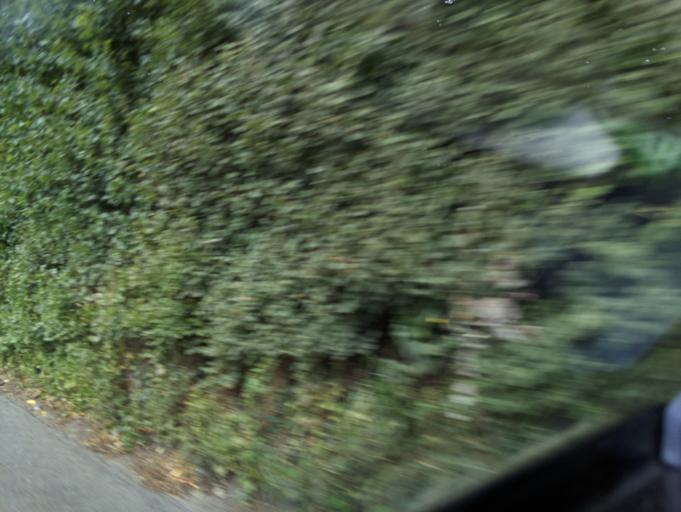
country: GB
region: England
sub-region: Somerset
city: Glastonbury
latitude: 51.1007
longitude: -2.6880
